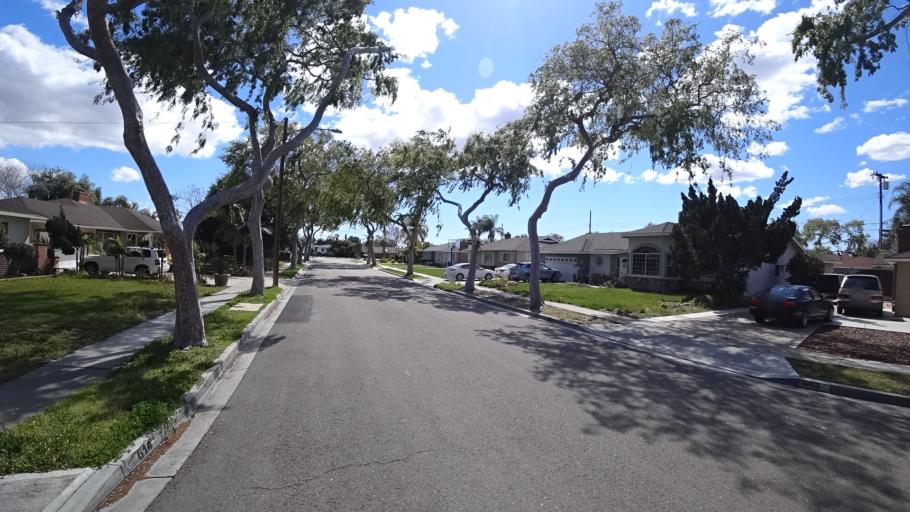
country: US
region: California
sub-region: Orange County
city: Anaheim
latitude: 33.8318
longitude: -117.8968
